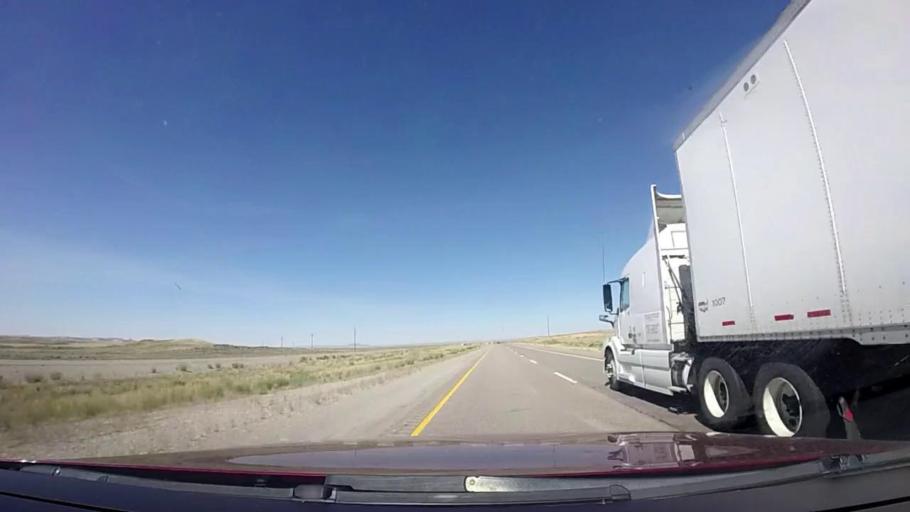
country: US
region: Wyoming
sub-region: Sweetwater County
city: Rock Springs
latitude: 41.6327
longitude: -108.3627
